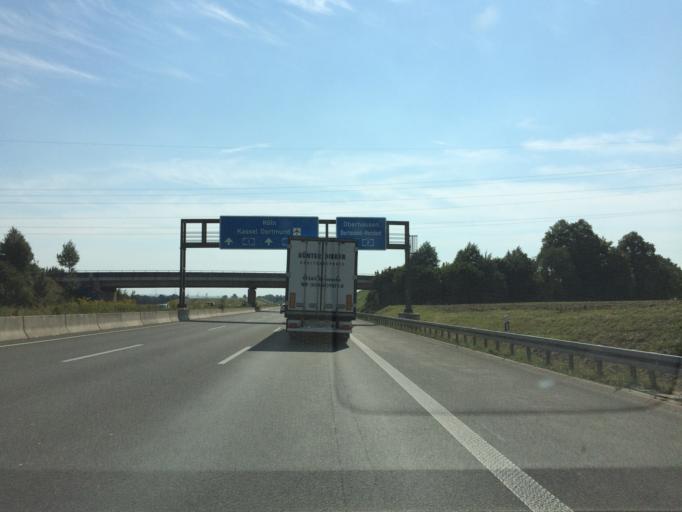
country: DE
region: North Rhine-Westphalia
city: Kamen
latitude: 51.6082
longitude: 7.6889
